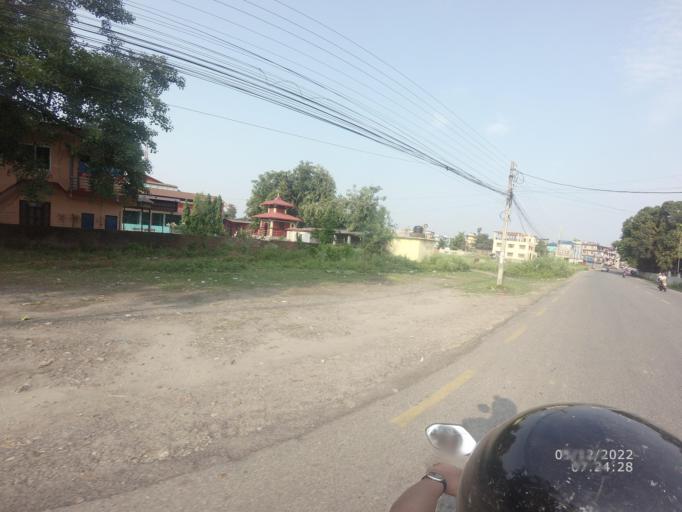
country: NP
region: Central Region
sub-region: Narayani Zone
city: Bharatpur
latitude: 27.6803
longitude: 84.4362
